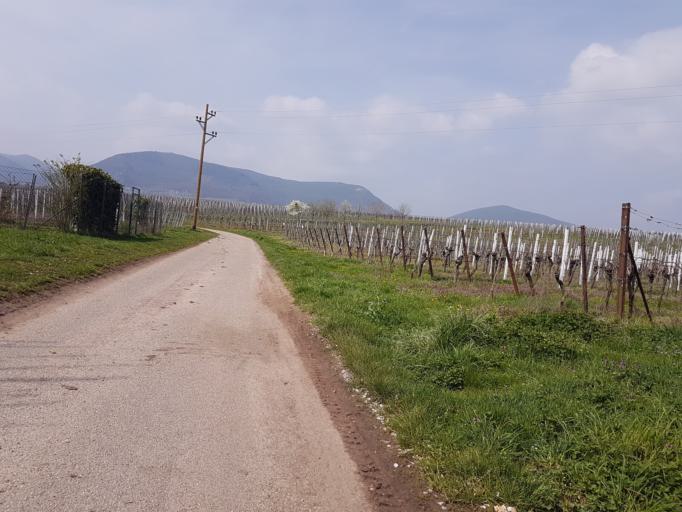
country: DE
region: Rheinland-Pfalz
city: Roschbach
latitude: 49.2589
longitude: 8.1188
